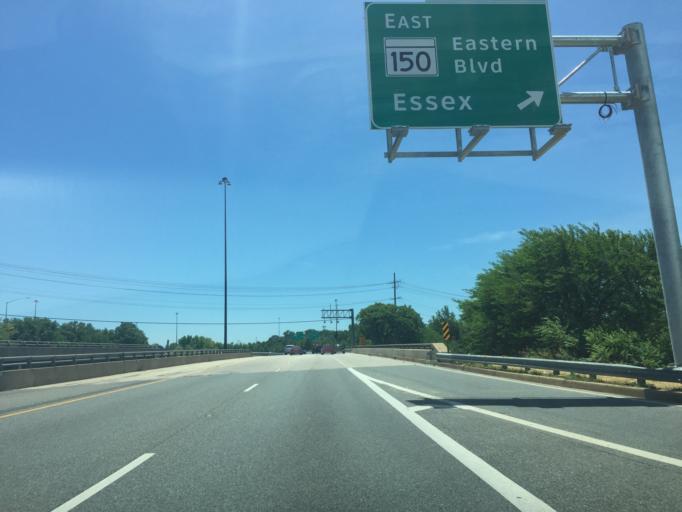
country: US
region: Maryland
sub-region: Baltimore County
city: Rosedale
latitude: 39.2981
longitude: -76.5028
